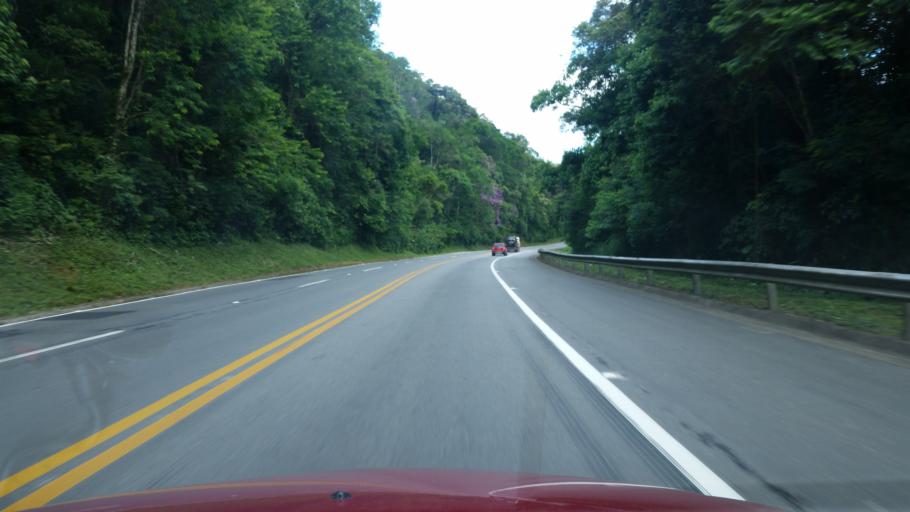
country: BR
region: Sao Paulo
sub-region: Miracatu
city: Miracatu
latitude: -24.2665
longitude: -47.2725
